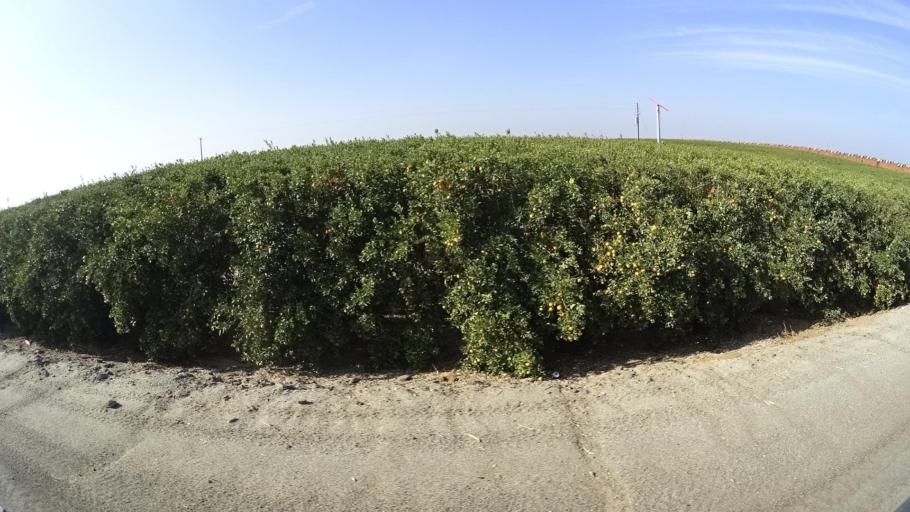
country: US
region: California
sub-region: Kern County
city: McFarland
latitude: 35.6372
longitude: -119.1335
